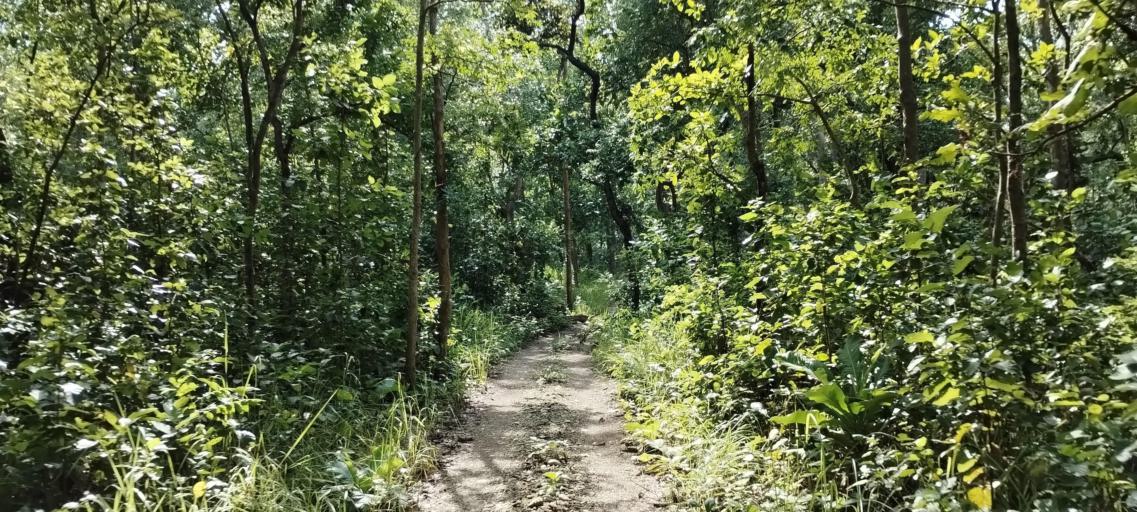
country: NP
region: Far Western
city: Tikapur
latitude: 28.5650
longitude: 81.2800
